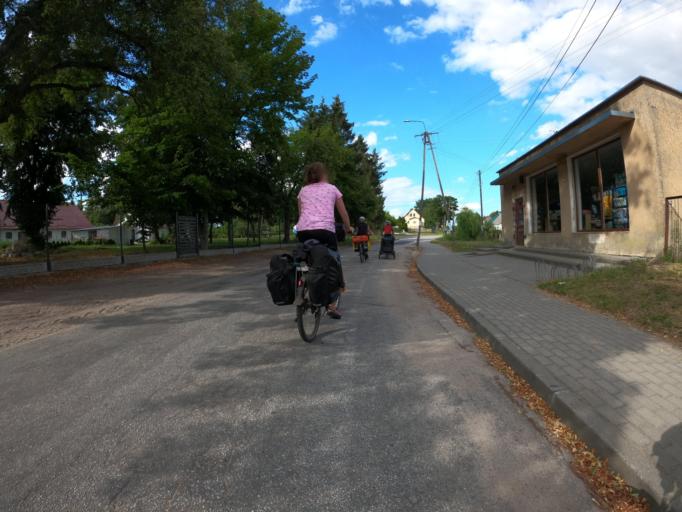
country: PL
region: West Pomeranian Voivodeship
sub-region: Powiat swidwinski
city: Swidwin
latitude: 53.7583
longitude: 15.6718
